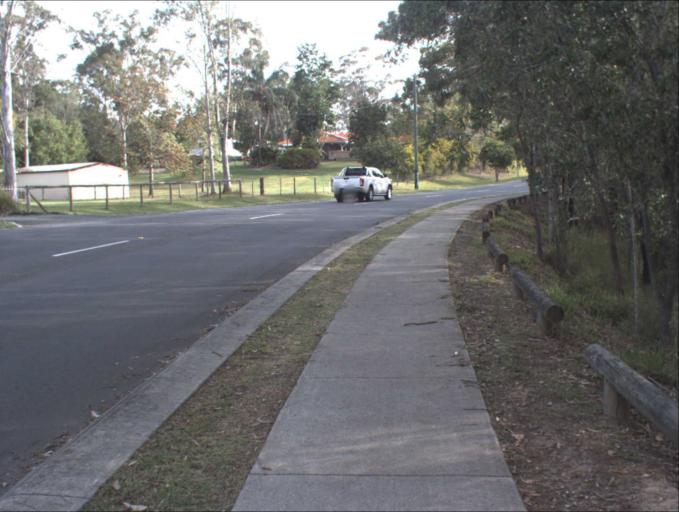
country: AU
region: Queensland
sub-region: Brisbane
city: Forest Lake
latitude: -27.6639
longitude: 152.9980
